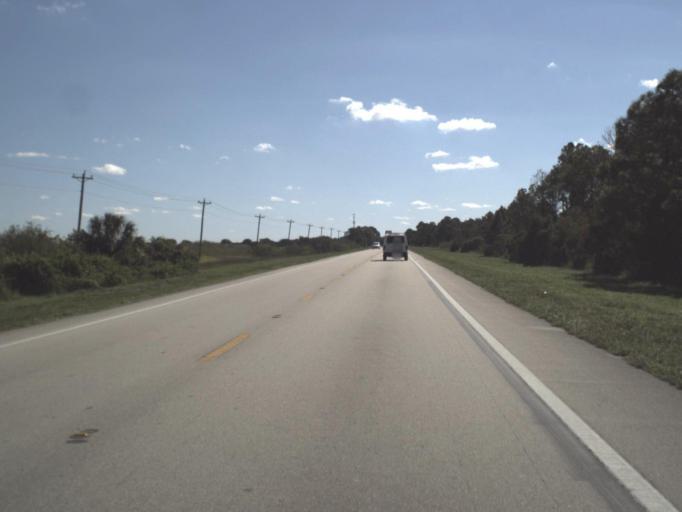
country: US
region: Florida
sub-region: Lee County
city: Lehigh Acres
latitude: 26.5168
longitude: -81.5572
